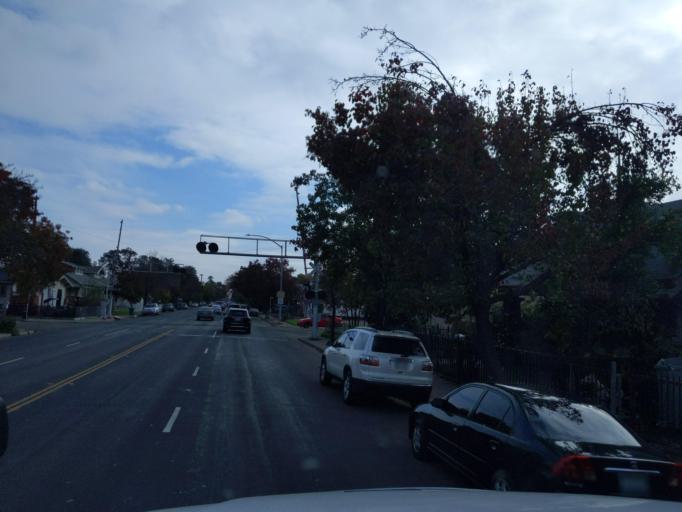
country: US
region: California
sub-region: San Joaquin County
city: Stockton
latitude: 37.9673
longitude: -121.2775
